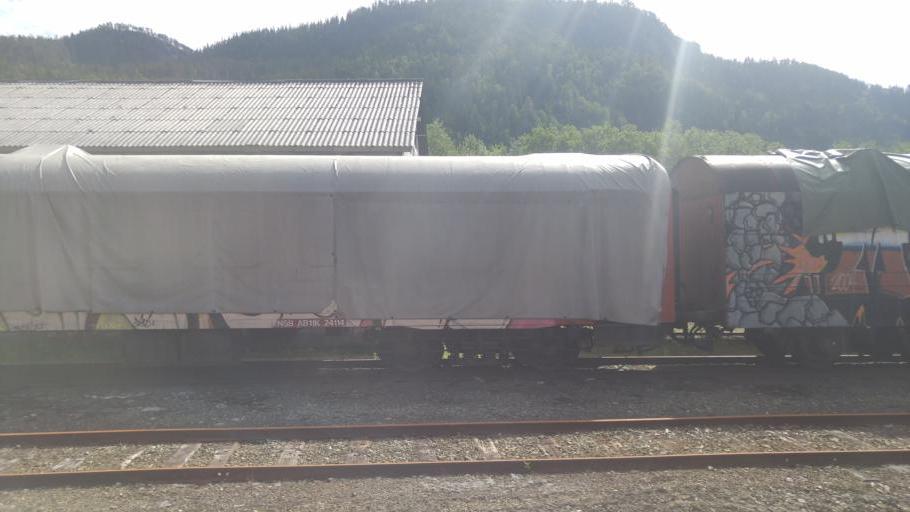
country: NO
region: Sor-Trondelag
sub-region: Midtre Gauldal
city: Storen
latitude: 63.0574
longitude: 10.2873
